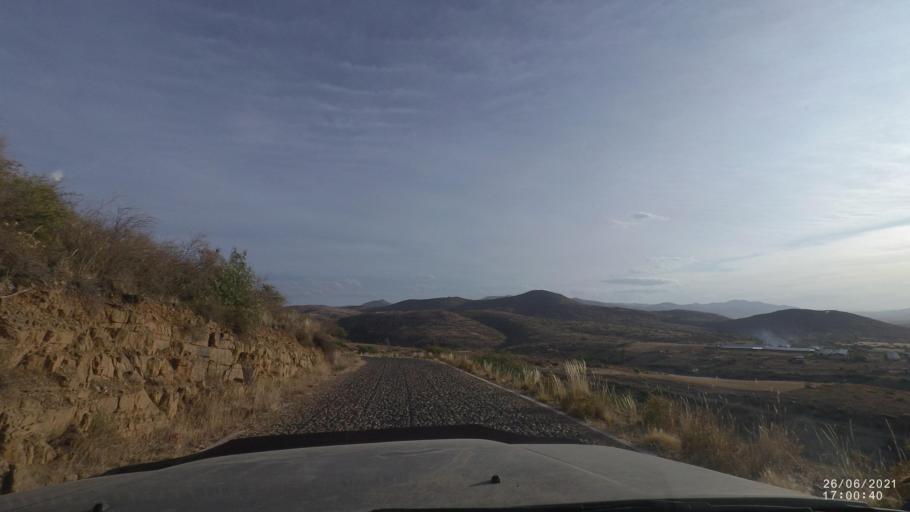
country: BO
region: Cochabamba
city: Cliza
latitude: -17.6614
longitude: -65.9086
